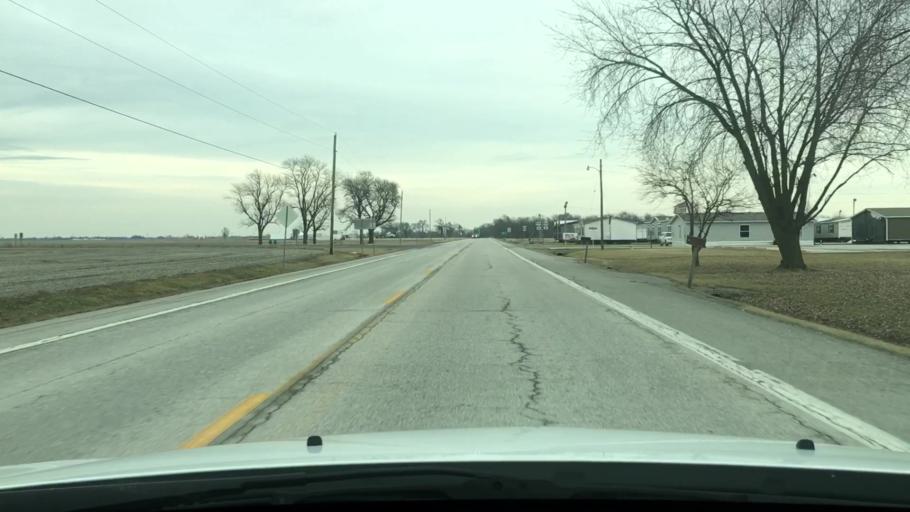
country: US
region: Missouri
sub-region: Audrain County
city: Vandalia
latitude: 39.2792
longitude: -91.5744
